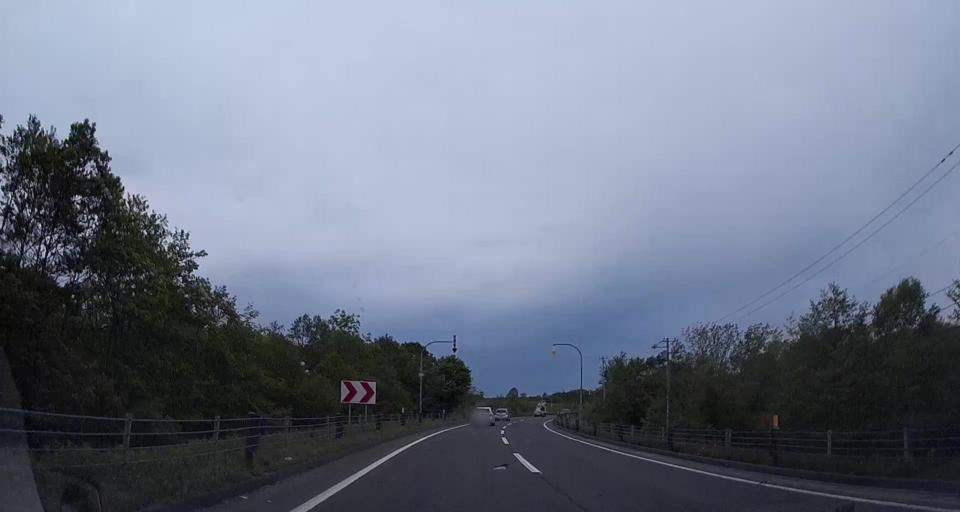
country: JP
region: Hokkaido
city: Chitose
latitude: 42.6997
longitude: 141.7417
